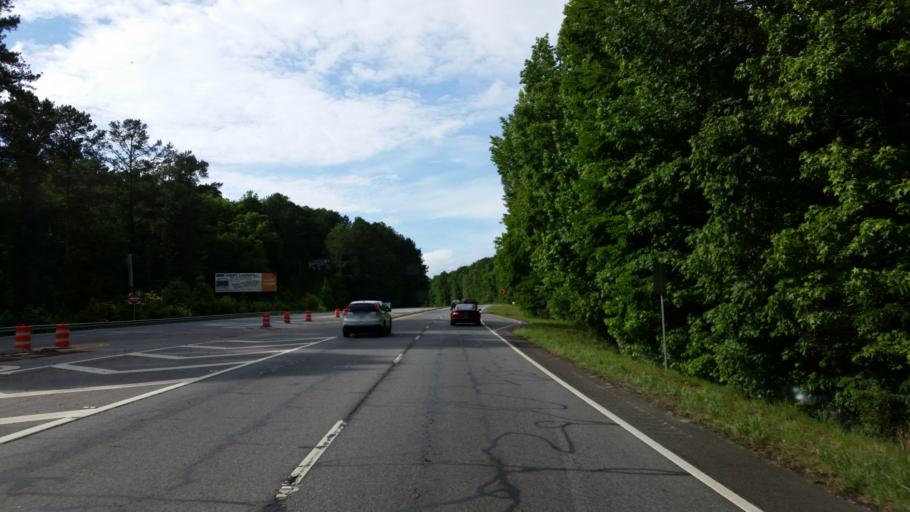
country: US
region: Georgia
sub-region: Bartow County
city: Emerson
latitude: 34.0928
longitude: -84.7401
